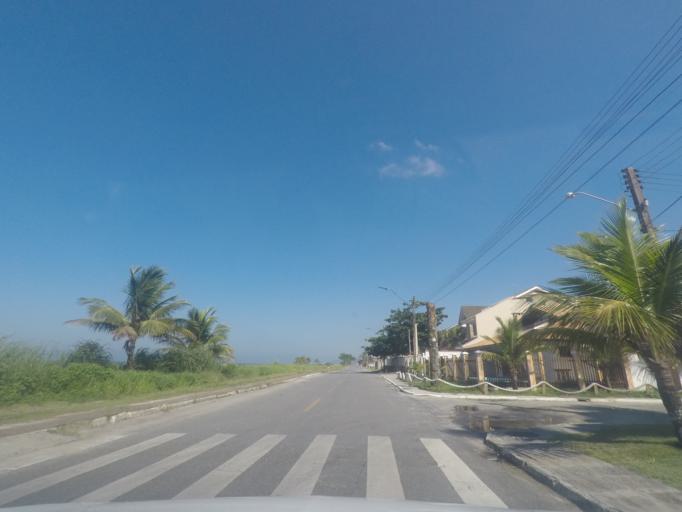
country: BR
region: Parana
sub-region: Pontal Do Parana
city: Pontal do Parana
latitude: -25.7374
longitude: -48.4928
